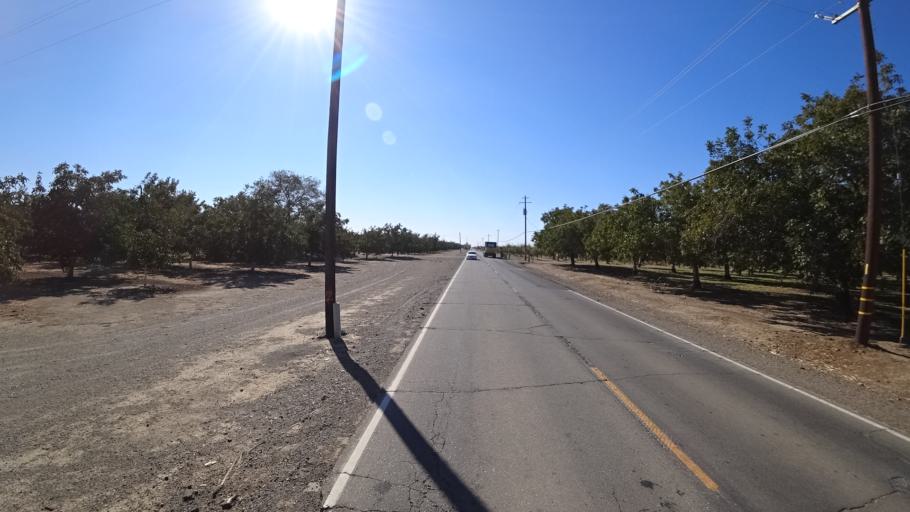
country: US
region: California
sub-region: Yolo County
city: Winters
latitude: 38.5809
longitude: -121.9714
